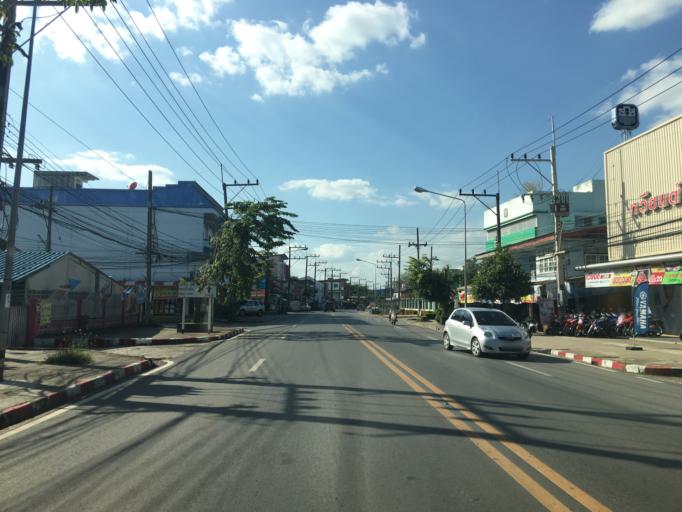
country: TH
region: Phayao
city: Chun
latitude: 19.3415
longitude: 100.1233
